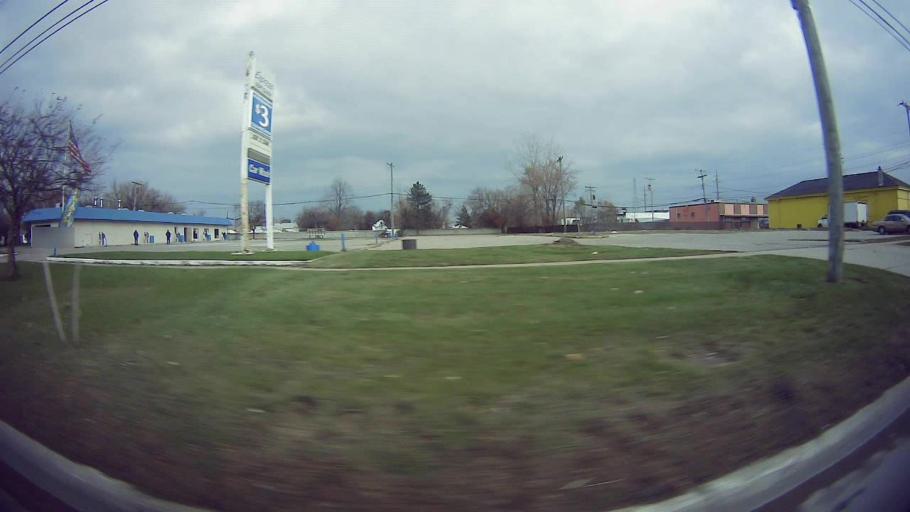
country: US
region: Michigan
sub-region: Macomb County
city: Eastpointe
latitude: 42.4791
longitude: -82.9867
